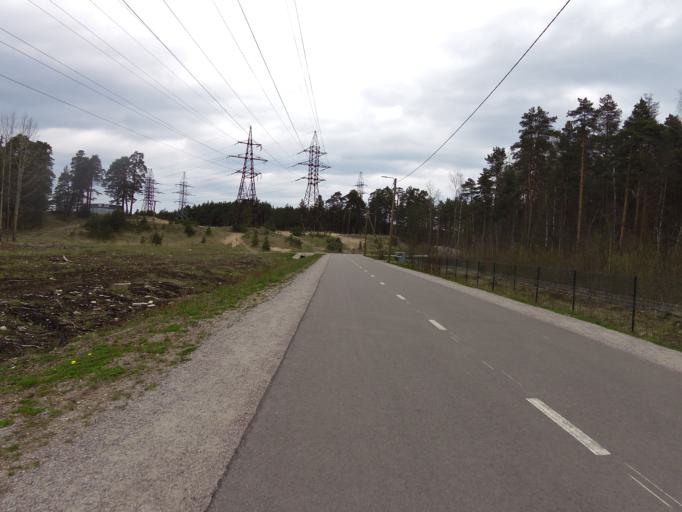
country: EE
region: Harju
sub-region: Tallinna linn
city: Tallinn
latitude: 59.3942
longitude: 24.7316
